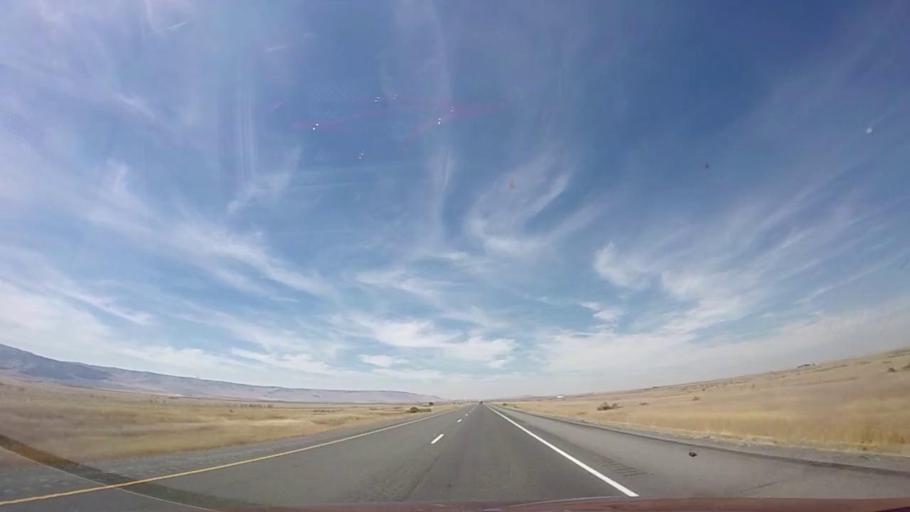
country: US
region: Idaho
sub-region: Minidoka County
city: Rupert
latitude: 42.3866
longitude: -113.2855
